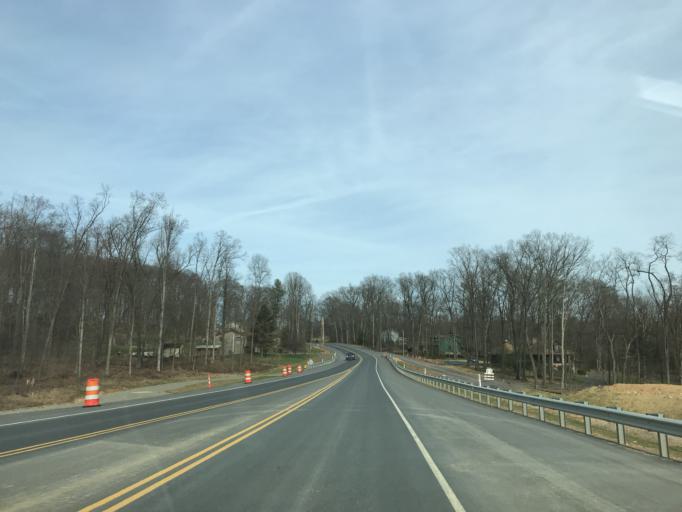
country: US
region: Pennsylvania
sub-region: Northumberland County
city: Northumberland
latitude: 40.9178
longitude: -76.8339
